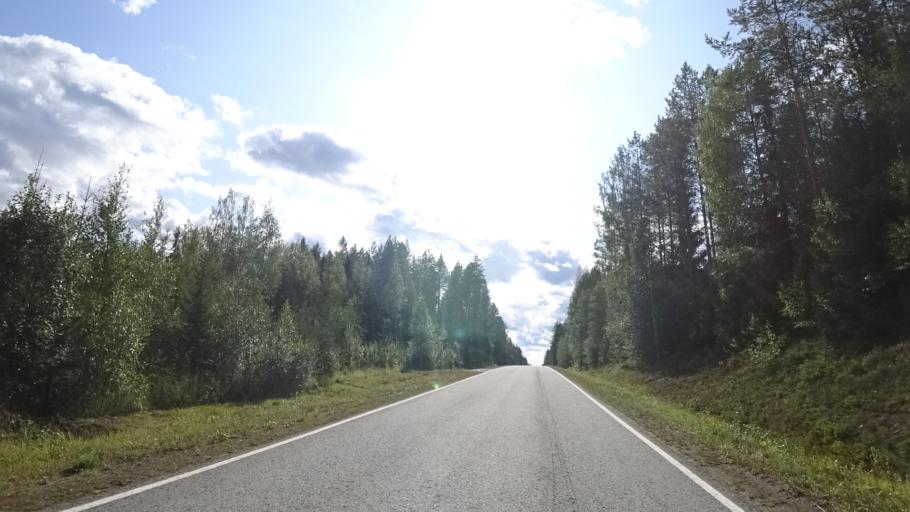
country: RU
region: Republic of Karelia
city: Vyartsilya
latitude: 62.2488
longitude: 30.7256
